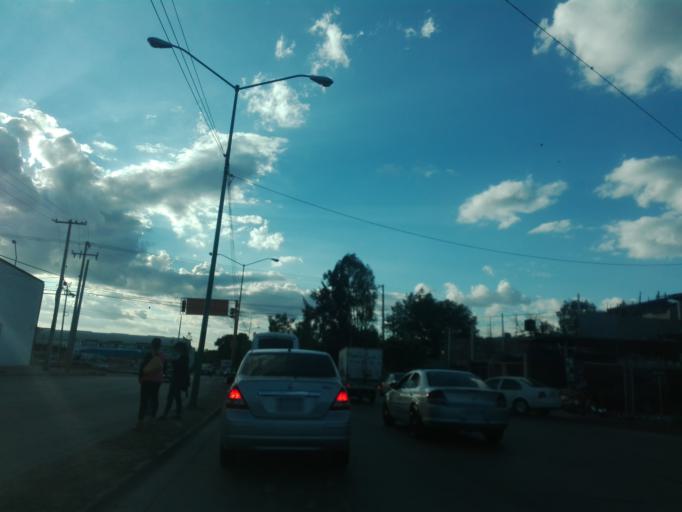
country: MX
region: Guanajuato
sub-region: Leon
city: San Jose de Duran (Los Troncoso)
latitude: 21.0913
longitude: -101.6786
